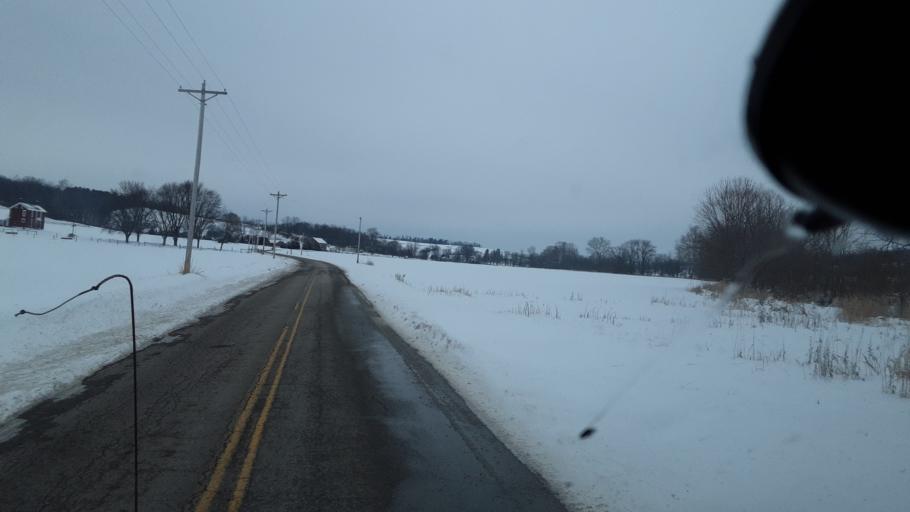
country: US
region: Ohio
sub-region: Perry County
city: Somerset
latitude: 39.8874
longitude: -82.2170
